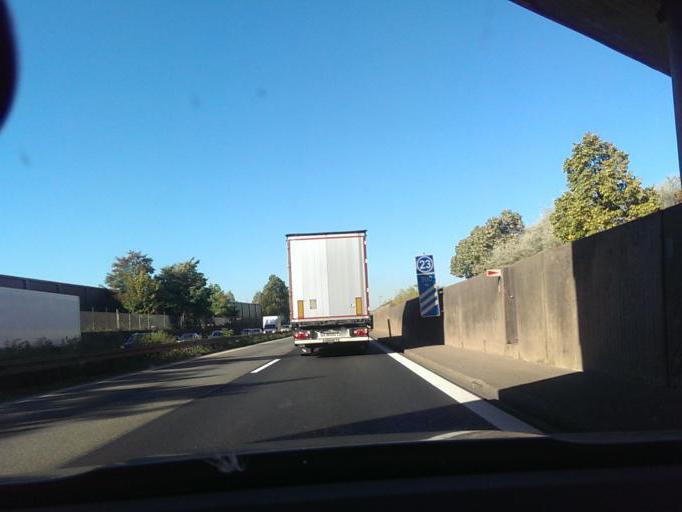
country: DE
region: Baden-Wuerttemberg
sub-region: Regierungsbezirk Stuttgart
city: Sindelfingen
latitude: 48.6941
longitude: 9.0084
